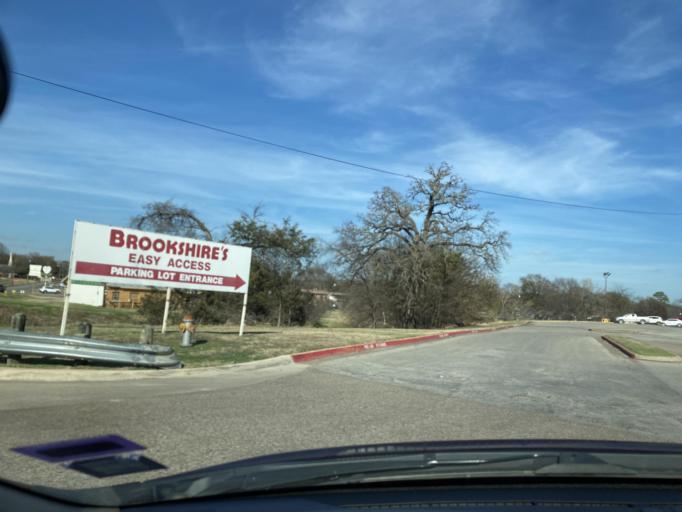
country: US
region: Texas
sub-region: Navarro County
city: Corsicana
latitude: 32.0995
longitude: -96.4720
